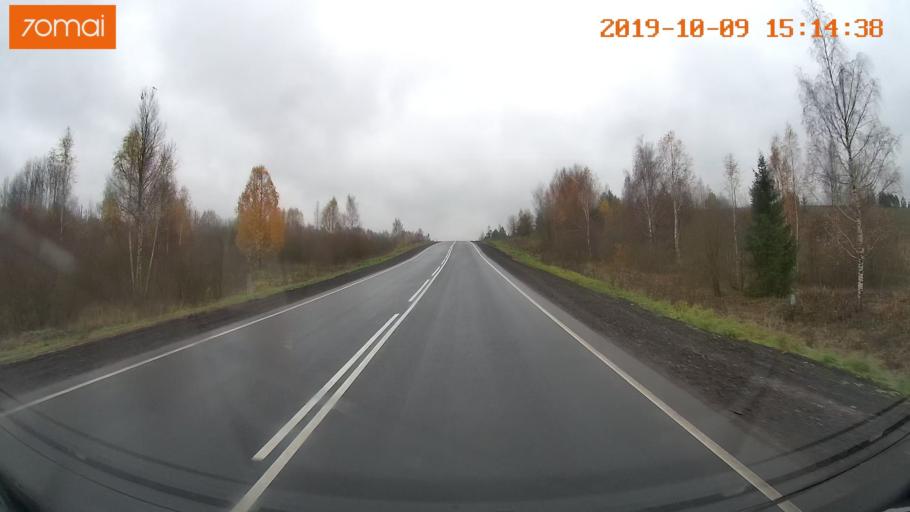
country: RU
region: Kostroma
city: Susanino
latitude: 58.1317
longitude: 41.6013
